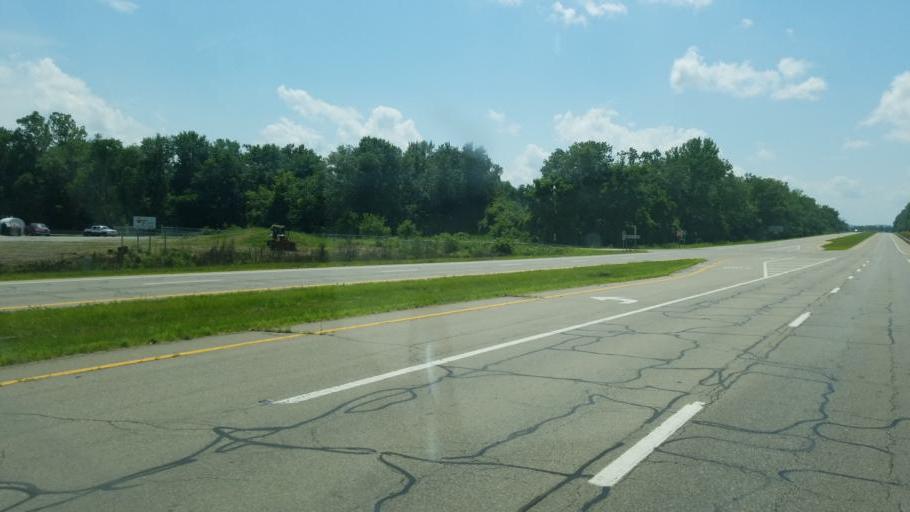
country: US
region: Ohio
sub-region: Tuscarawas County
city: Newcomerstown
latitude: 40.2831
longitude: -81.6390
